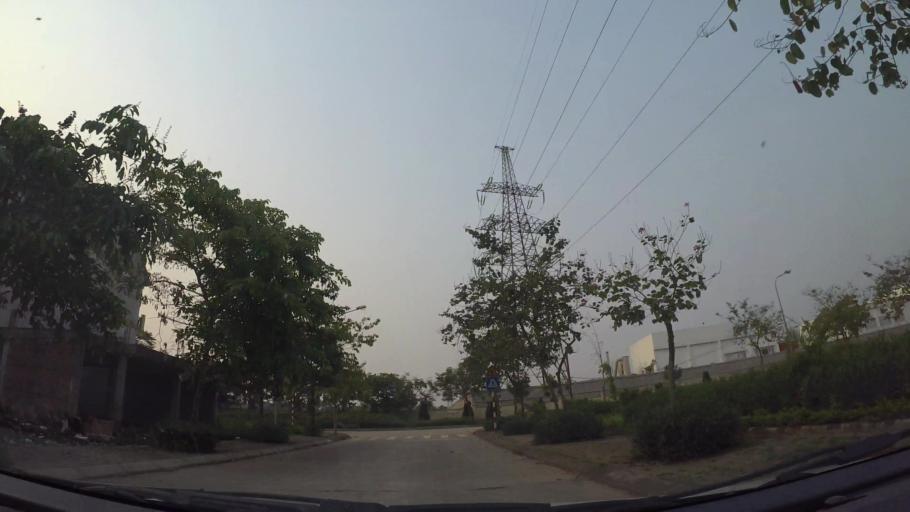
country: VN
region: Ha Noi
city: Cau Dien
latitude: 21.0079
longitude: 105.7342
